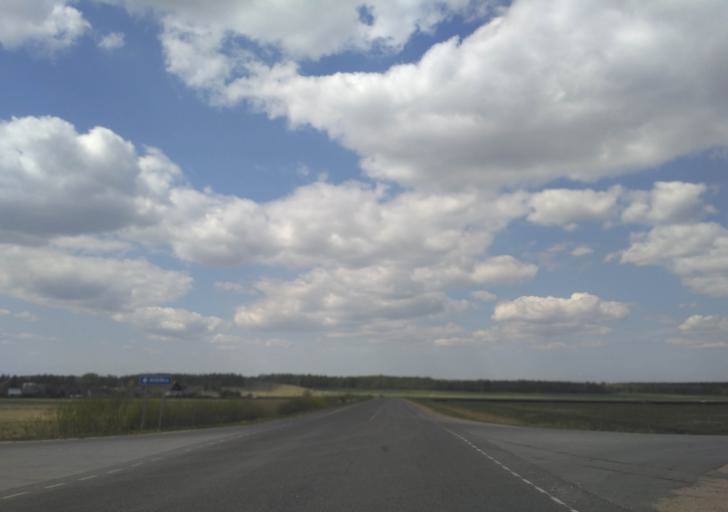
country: BY
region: Minsk
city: Vilyeyka
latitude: 54.5190
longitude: 26.9755
